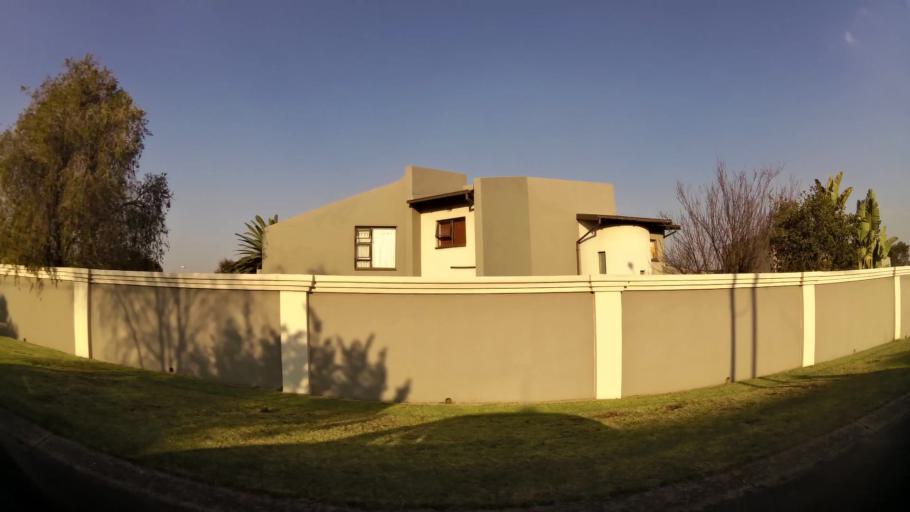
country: ZA
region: Gauteng
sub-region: City of Johannesburg Metropolitan Municipality
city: Modderfontein
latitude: -26.0777
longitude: 28.2171
